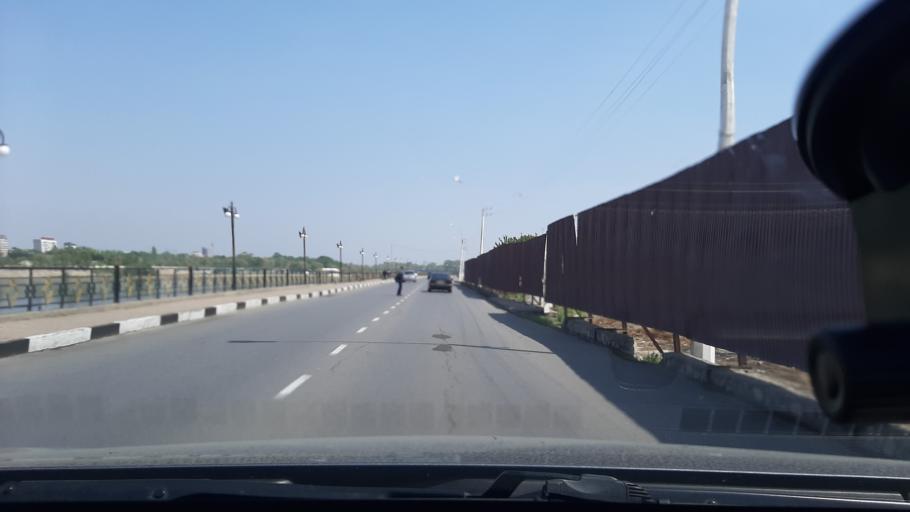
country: TJ
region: Viloyati Sughd
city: Khujand
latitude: 40.2923
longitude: 69.6295
